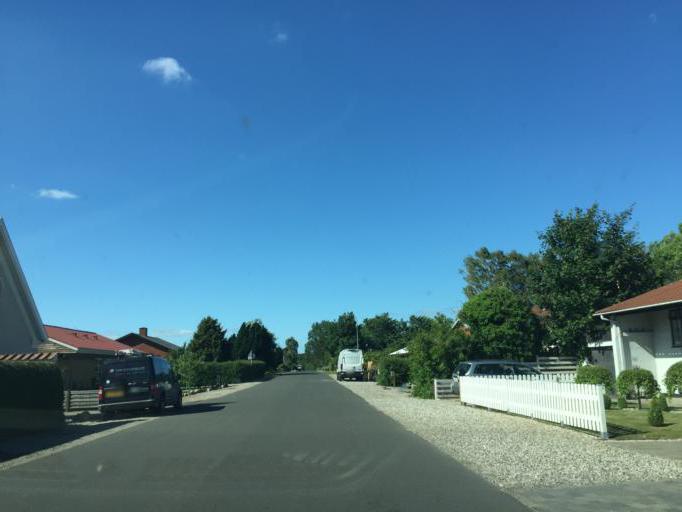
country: DK
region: South Denmark
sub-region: Odense Kommune
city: Hojby
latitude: 55.3403
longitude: 10.4382
